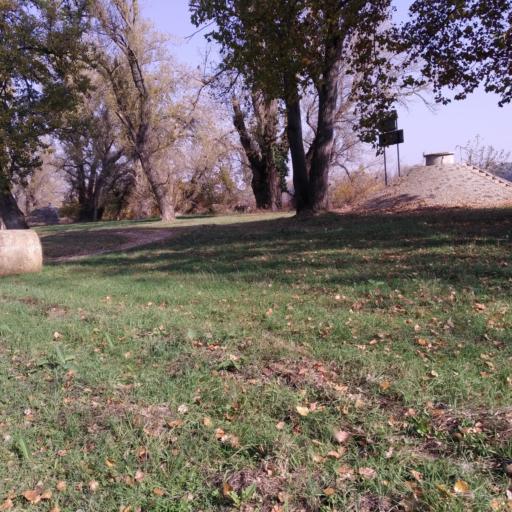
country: HU
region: Pest
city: Budakalasz
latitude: 47.5925
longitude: 19.0739
